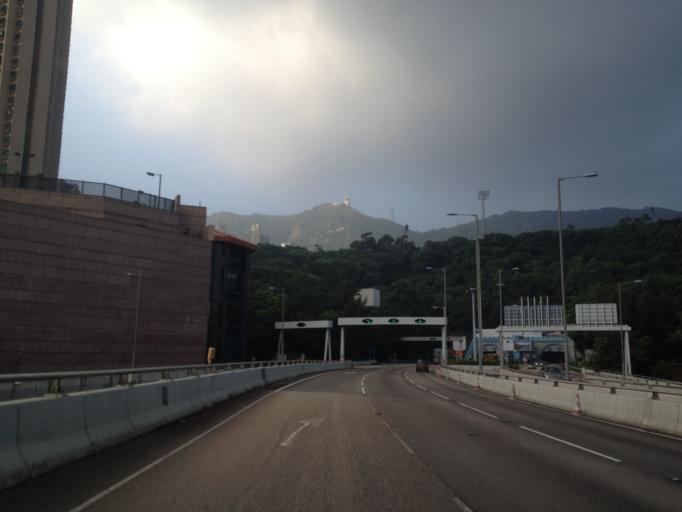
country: HK
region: Wong Tai Sin
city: Wong Tai Sin
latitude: 22.3394
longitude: 114.2033
